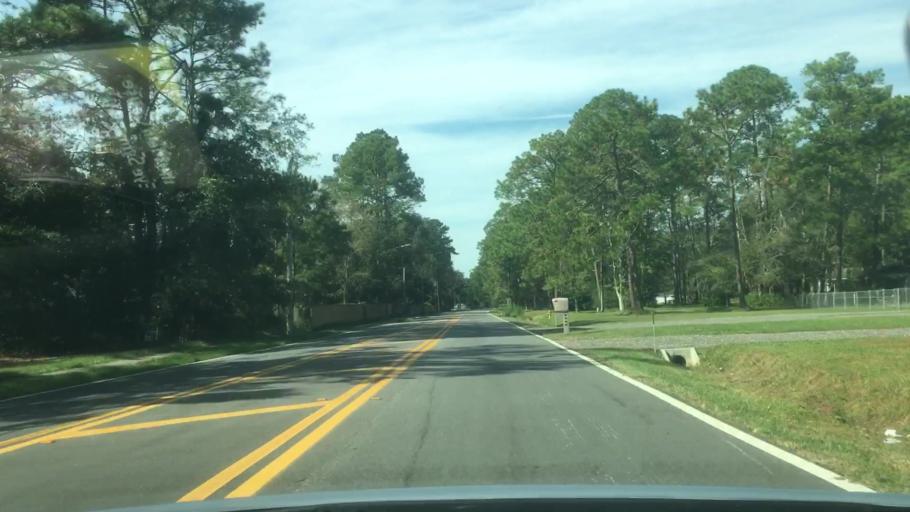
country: US
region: Florida
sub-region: Nassau County
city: Yulee
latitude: 30.4842
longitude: -81.5970
